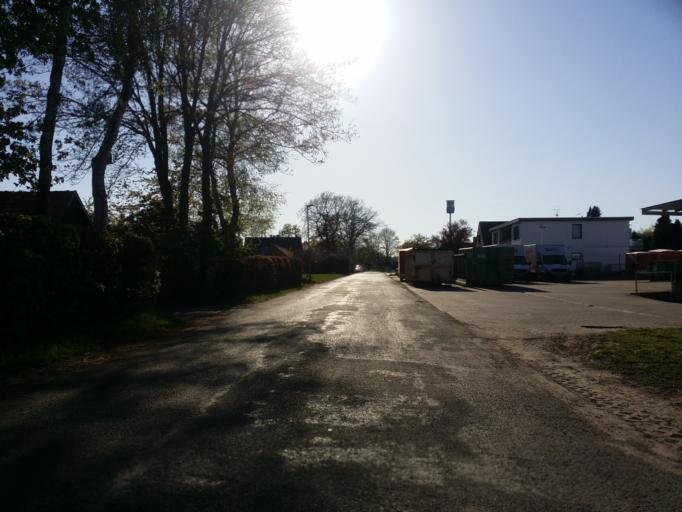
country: DE
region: Lower Saxony
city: Stuhr
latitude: 53.0109
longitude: 8.7085
